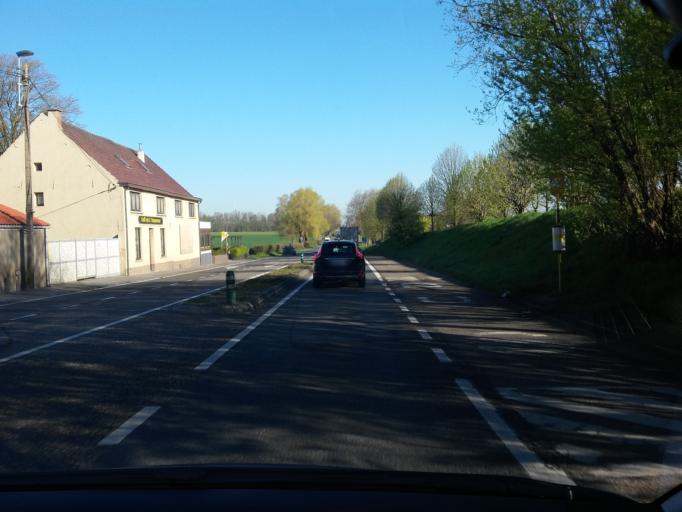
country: BE
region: Wallonia
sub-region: Province du Brabant Wallon
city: Waterloo
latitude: 50.6810
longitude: 4.4116
